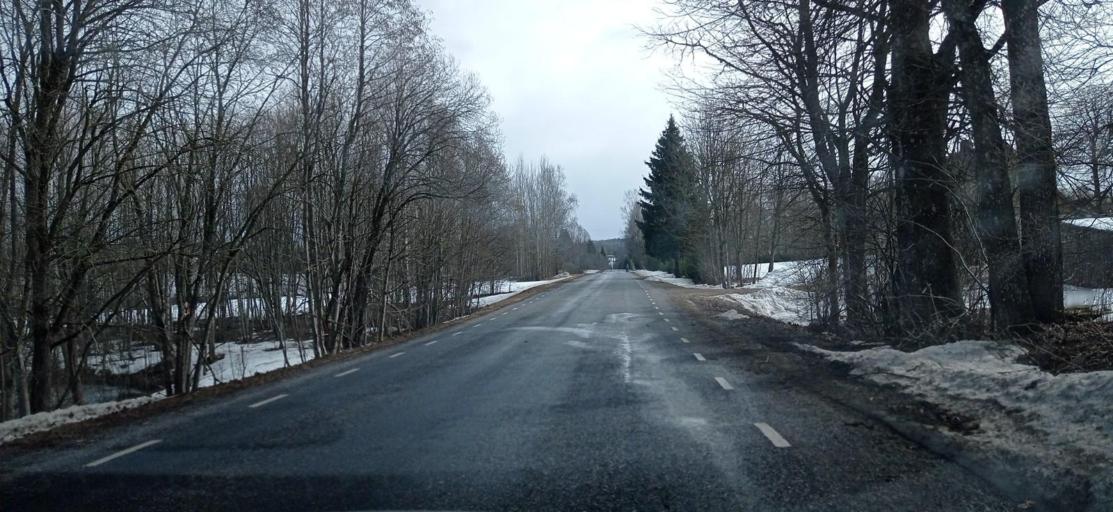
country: EE
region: Tartu
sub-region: UElenurme vald
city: Ulenurme
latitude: 58.0717
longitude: 26.7078
